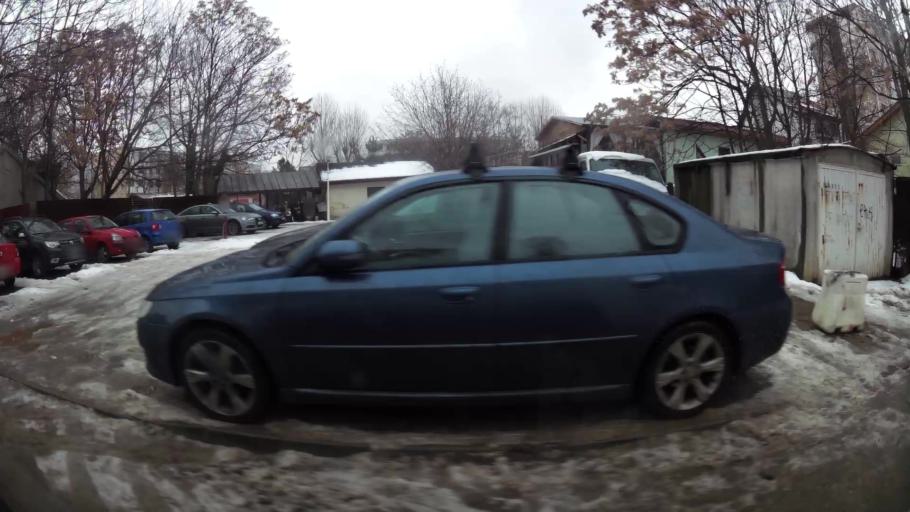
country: RO
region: Ilfov
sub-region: Comuna Chiajna
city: Rosu
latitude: 44.4369
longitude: 26.0385
